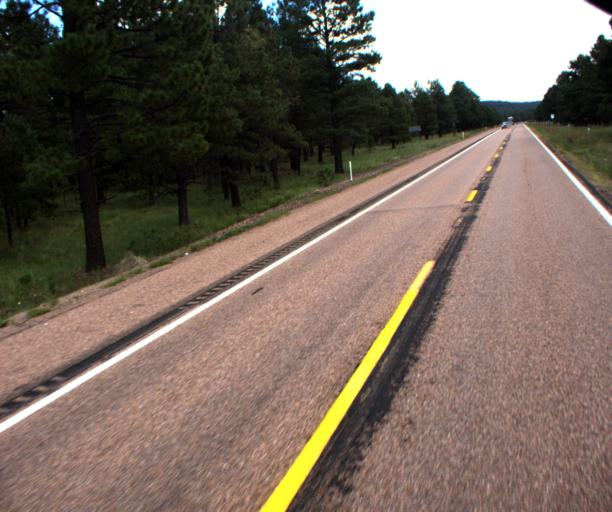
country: US
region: Arizona
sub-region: Navajo County
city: Pinetop-Lakeside
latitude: 34.0442
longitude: -109.6920
